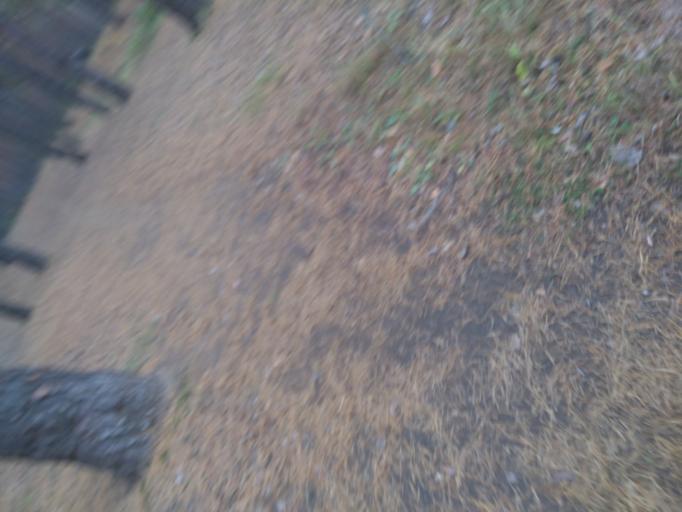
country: RU
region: Tatarstan
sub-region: Tukayevskiy Rayon
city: Naberezhnyye Chelny
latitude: 55.7543
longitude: 52.3831
